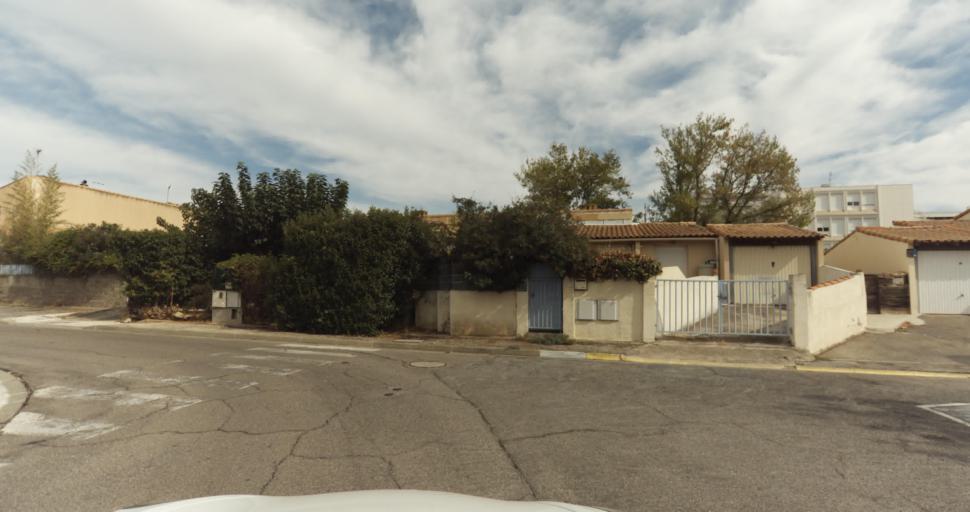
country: FR
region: Provence-Alpes-Cote d'Azur
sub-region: Departement des Bouches-du-Rhone
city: Miramas
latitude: 43.5932
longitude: 5.0076
